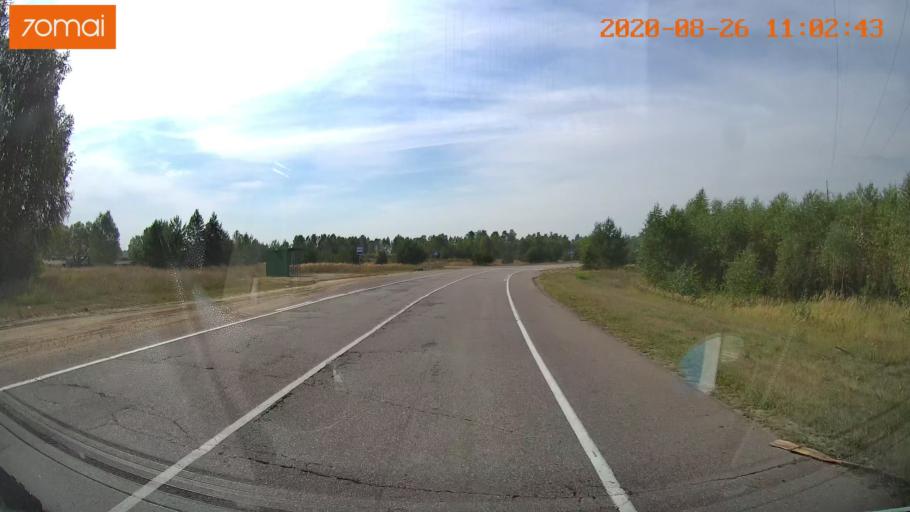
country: RU
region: Rjazan
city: Izhevskoye
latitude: 54.5473
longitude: 41.2227
